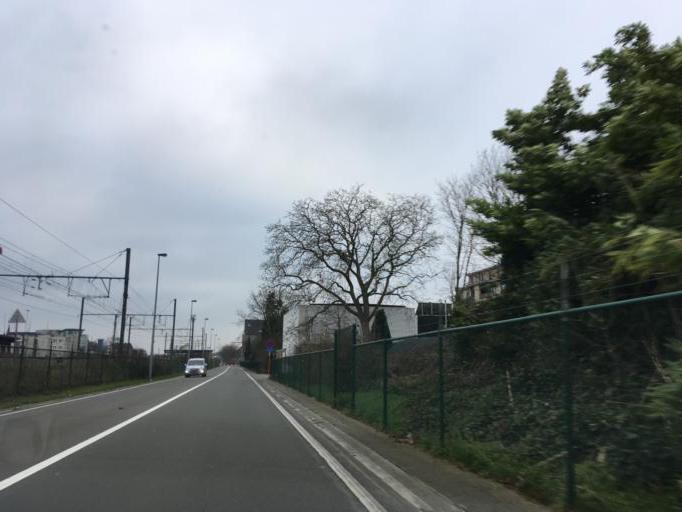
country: BE
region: Flanders
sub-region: Provincie West-Vlaanderen
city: Roeselare
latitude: 50.9544
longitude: 3.1285
